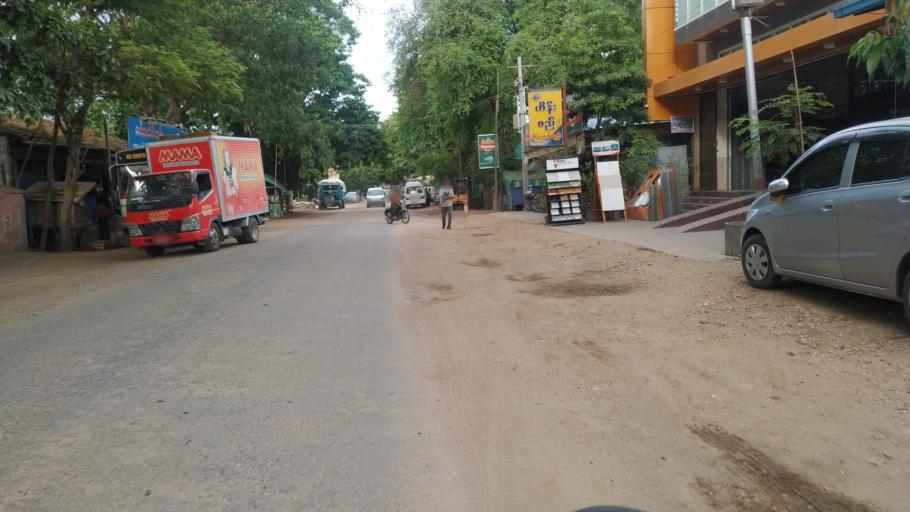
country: MM
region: Magway
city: Pakokku
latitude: 21.3356
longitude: 95.0763
